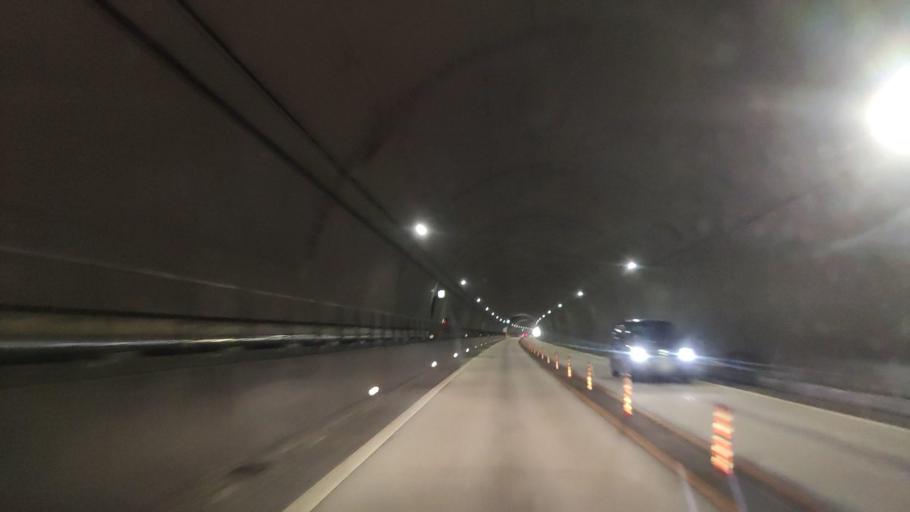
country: JP
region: Ehime
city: Hojo
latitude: 34.0814
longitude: 132.9768
